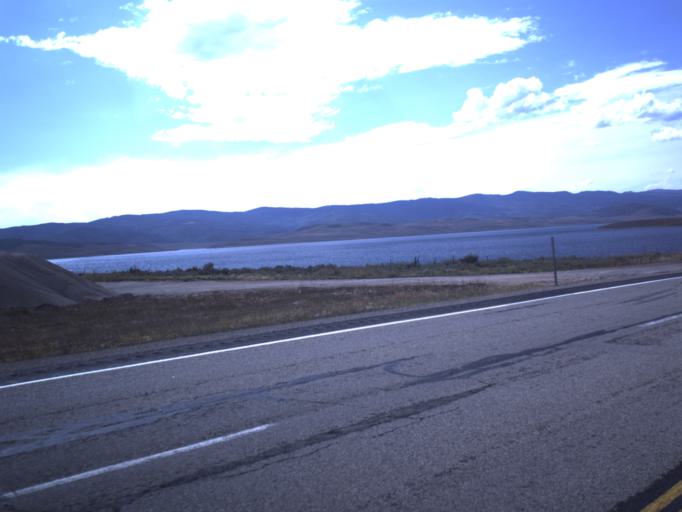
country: US
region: Utah
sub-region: Wasatch County
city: Heber
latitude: 40.1986
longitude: -111.1033
